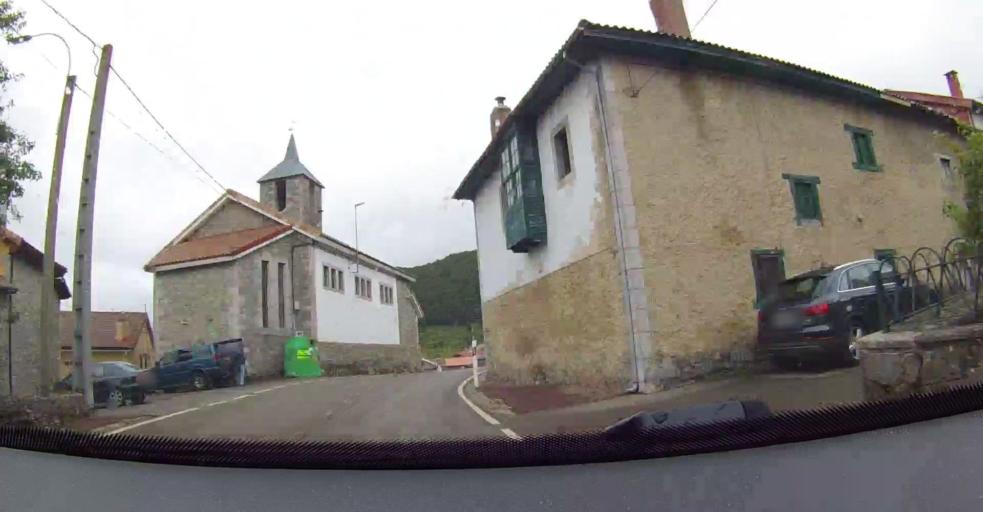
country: ES
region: Castille and Leon
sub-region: Provincia de Leon
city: Acebedo
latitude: 43.0646
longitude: -5.1374
